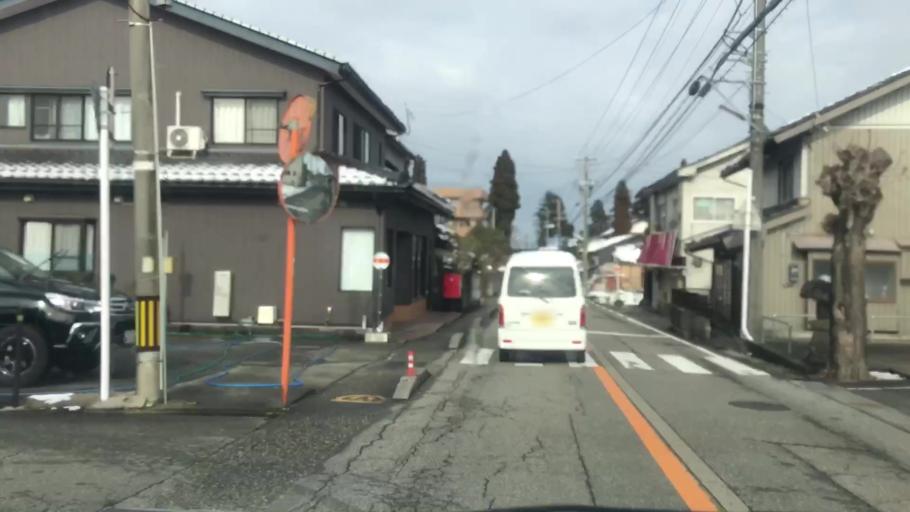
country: JP
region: Toyama
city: Toyama-shi
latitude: 36.6303
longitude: 137.2477
